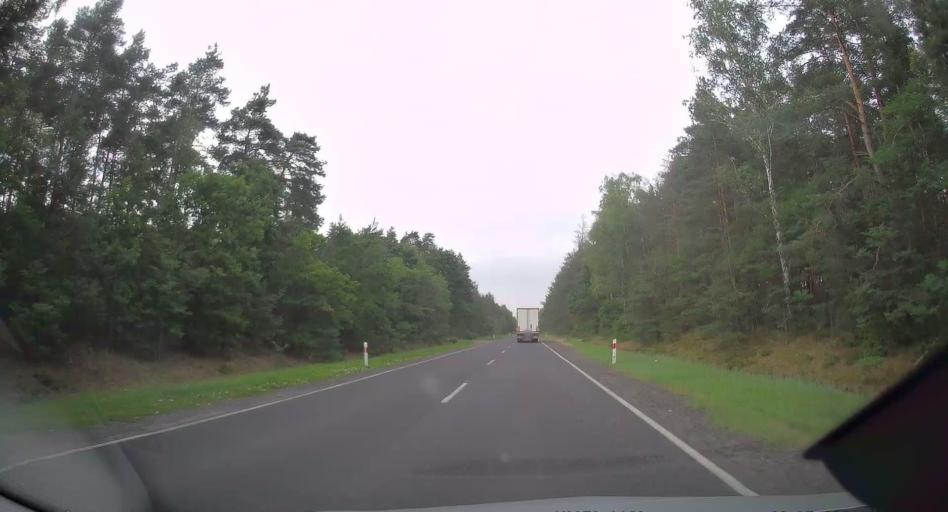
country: PL
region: Lodz Voivodeship
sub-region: Powiat radomszczanski
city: Plawno
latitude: 51.0007
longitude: 19.4177
